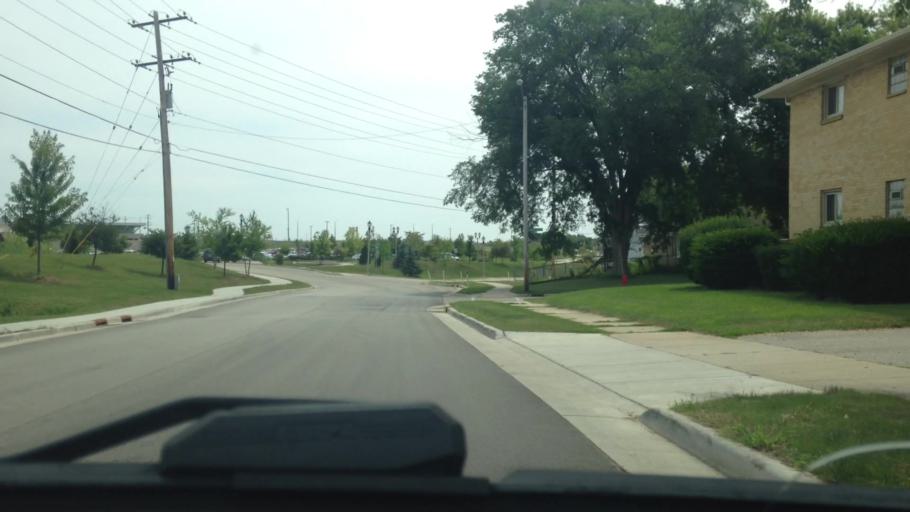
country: US
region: Wisconsin
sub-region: Waukesha County
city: Menomonee Falls
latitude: 43.1820
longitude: -88.1076
